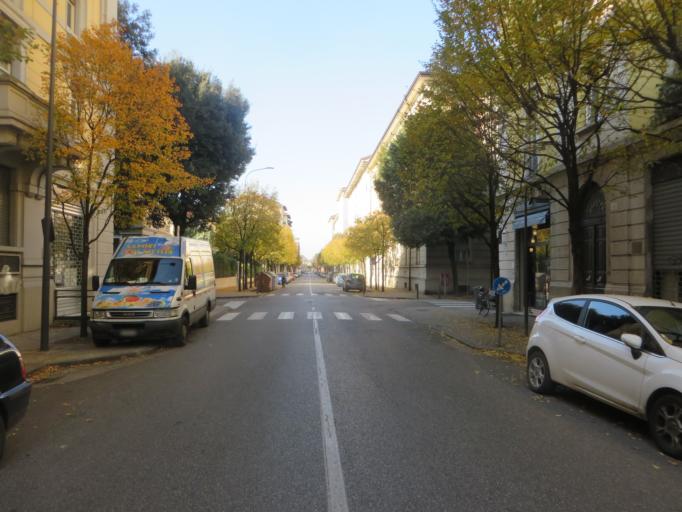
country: IT
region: Lombardy
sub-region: Provincia di Brescia
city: Brescia
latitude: 45.5489
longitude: 10.2173
